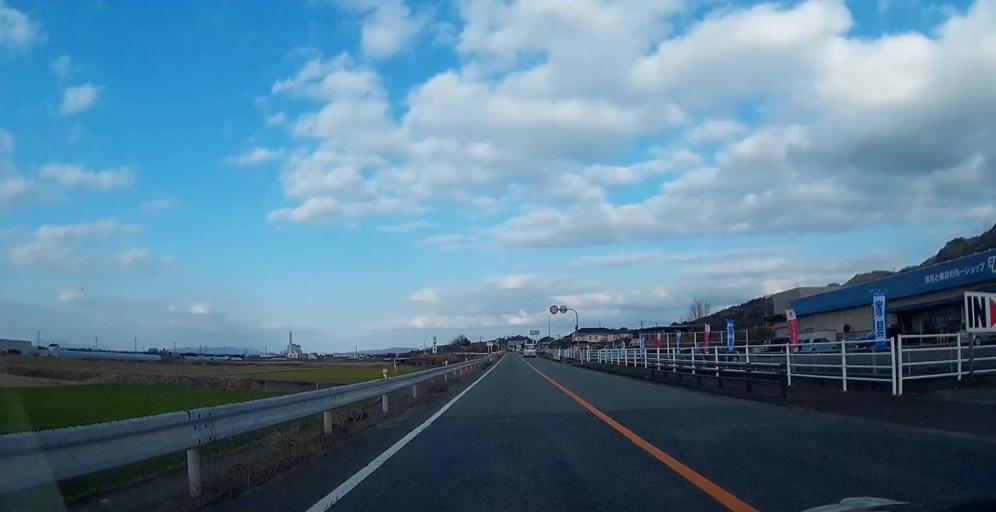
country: JP
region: Kumamoto
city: Yatsushiro
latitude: 32.5347
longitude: 130.6672
